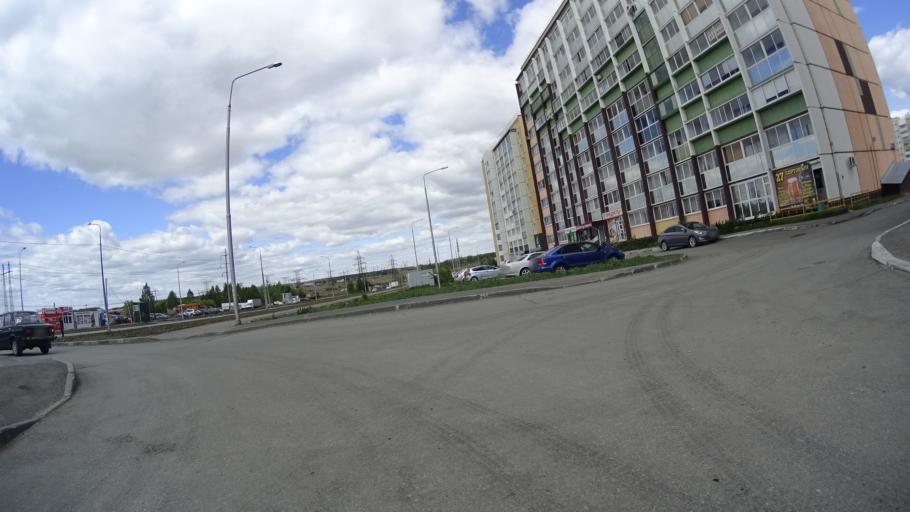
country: RU
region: Chelyabinsk
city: Roshchino
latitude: 55.1753
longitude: 61.2571
